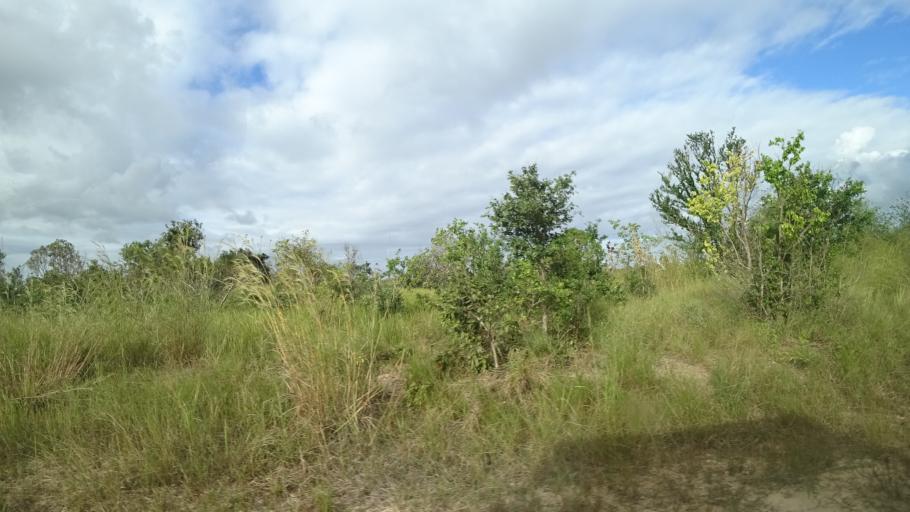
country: MZ
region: Sofala
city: Beira
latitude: -19.6368
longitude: 35.0594
